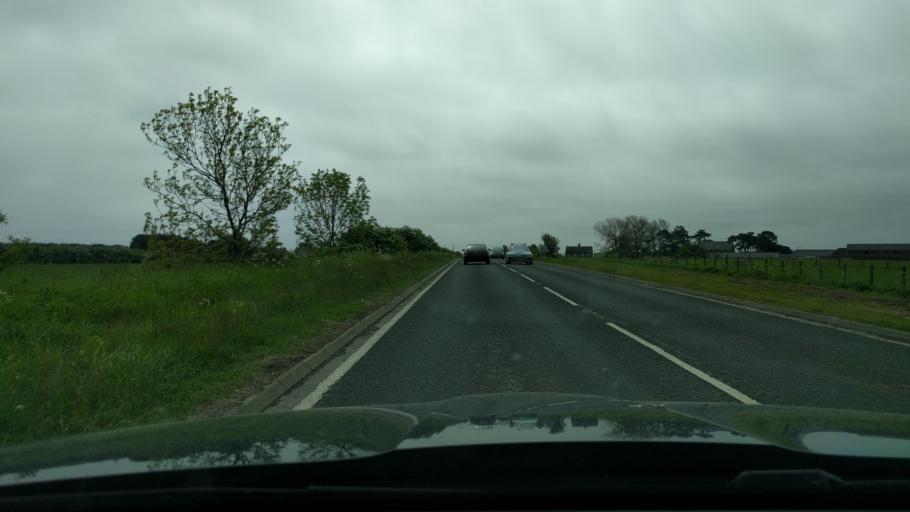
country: GB
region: England
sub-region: Northumberland
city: East Chevington
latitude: 55.2469
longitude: -1.5986
